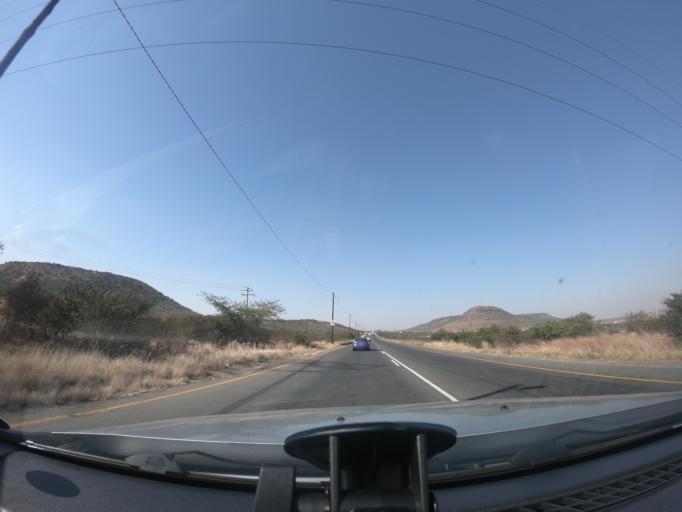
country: ZA
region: KwaZulu-Natal
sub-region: uThukela District Municipality
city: Ladysmith
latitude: -28.5542
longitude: 29.8356
